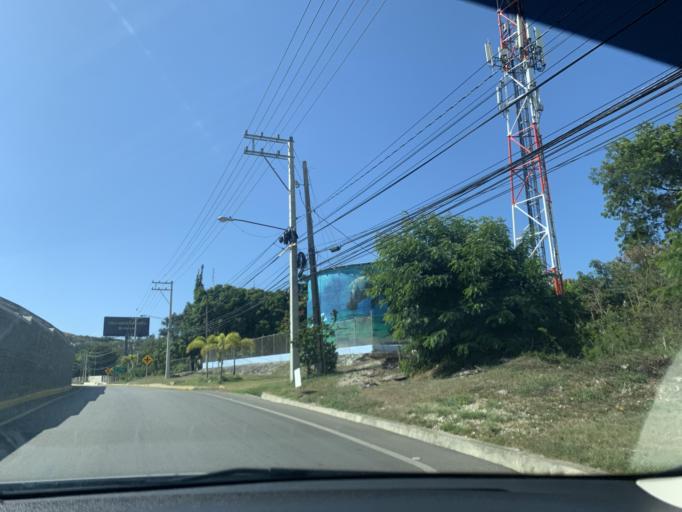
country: DO
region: Puerto Plata
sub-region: Puerto Plata
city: Puerto Plata
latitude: 19.8160
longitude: -70.7323
